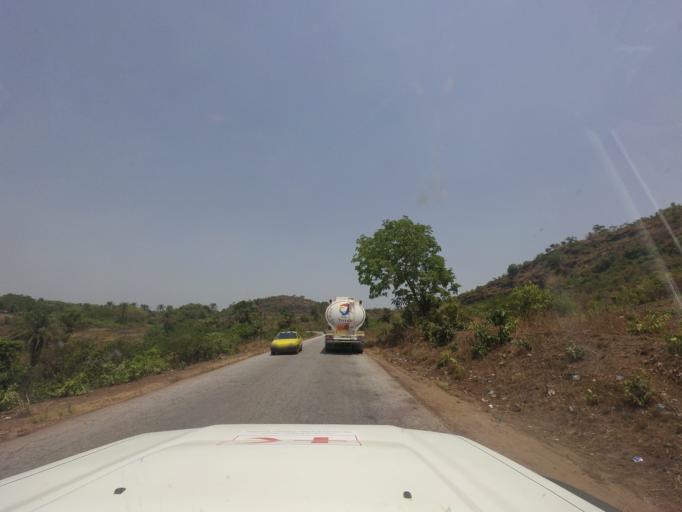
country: GN
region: Kindia
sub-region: Coyah
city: Coyah
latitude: 9.8347
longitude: -13.1379
